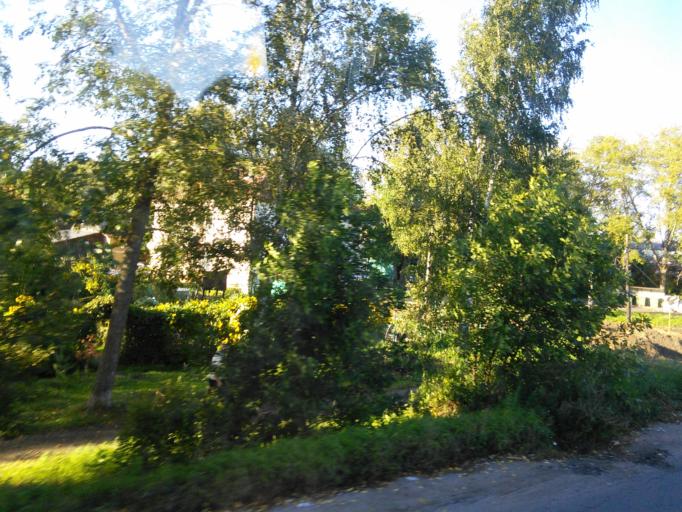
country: RU
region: Jaroslavl
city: Poshekhon'ye
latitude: 58.4991
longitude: 39.1088
